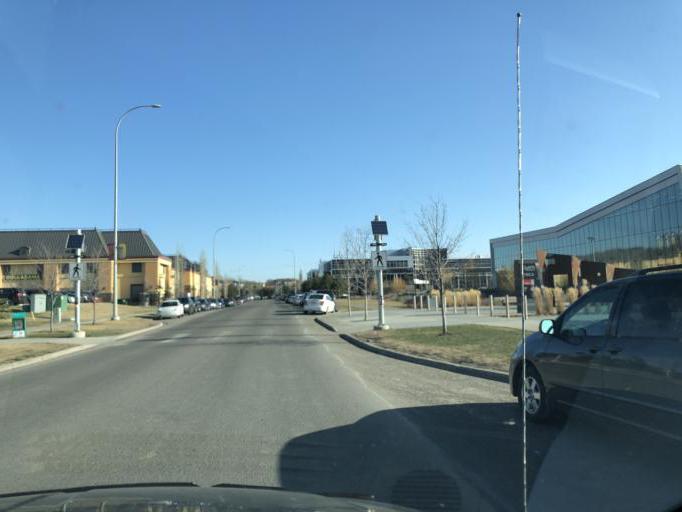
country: CA
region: Alberta
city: Calgary
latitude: 50.9609
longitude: -114.0072
